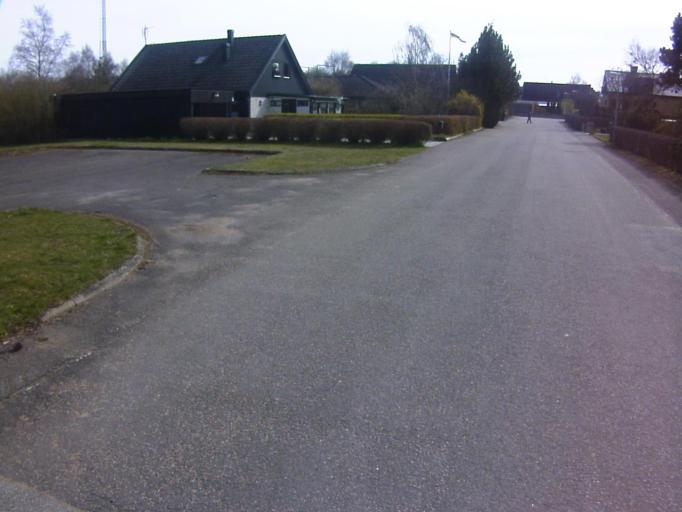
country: SE
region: Skane
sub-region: Kavlinge Kommun
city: Kaevlinge
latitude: 55.7812
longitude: 13.1107
